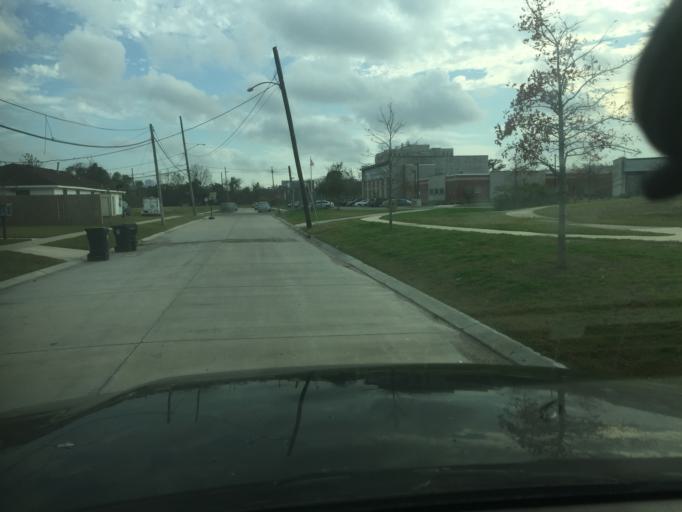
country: US
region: Louisiana
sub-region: Orleans Parish
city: New Orleans
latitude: 29.9953
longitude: -90.0829
